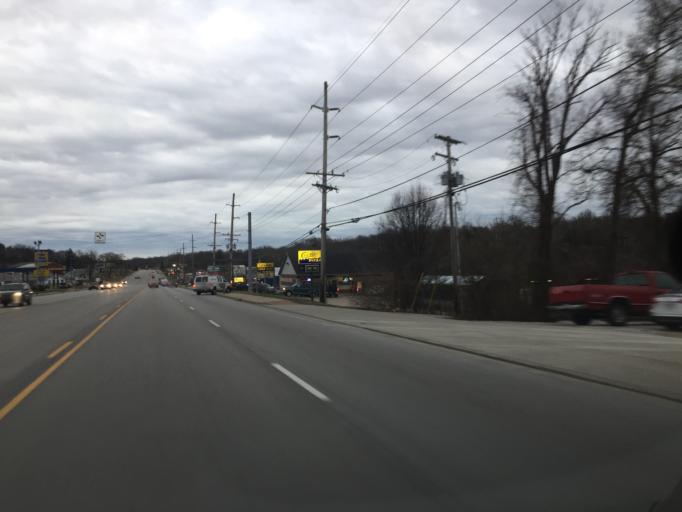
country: US
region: Indiana
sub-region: Monroe County
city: Ellettsville
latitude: 39.2221
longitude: -86.6075
